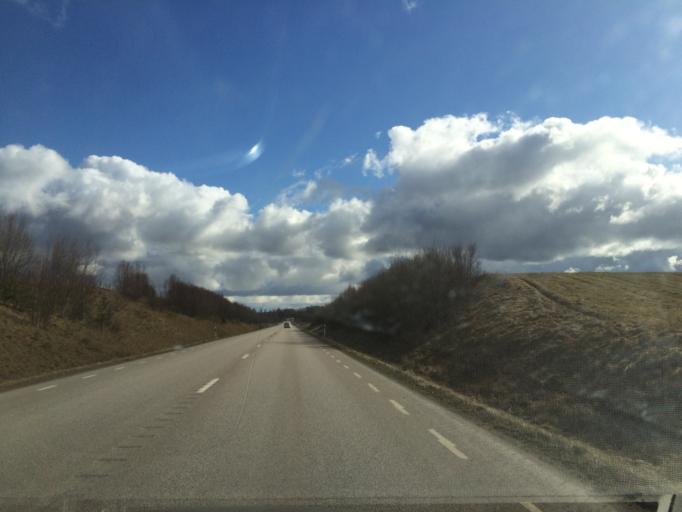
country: SE
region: Vaestra Goetaland
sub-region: Skara Kommun
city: Skara
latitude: 58.2946
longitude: 13.4731
